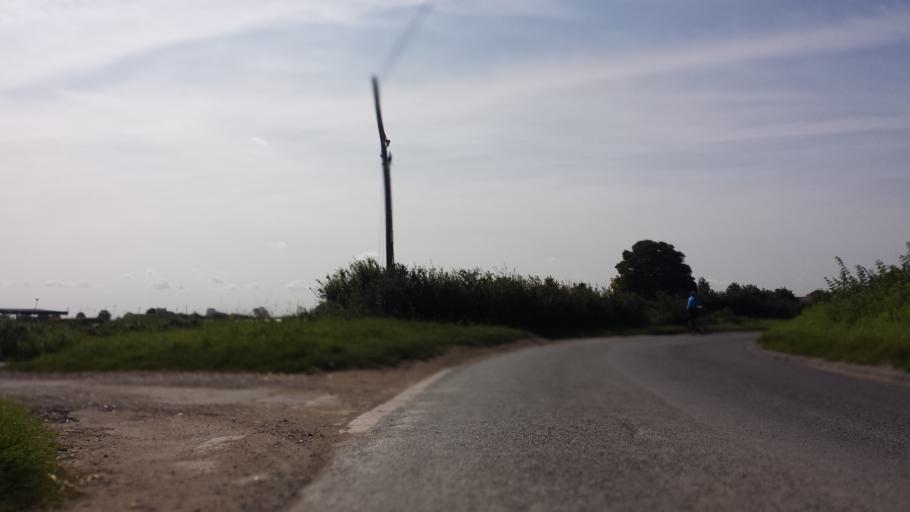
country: GB
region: England
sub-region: Cambridgeshire
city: Isleham
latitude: 52.3616
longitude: 0.4603
